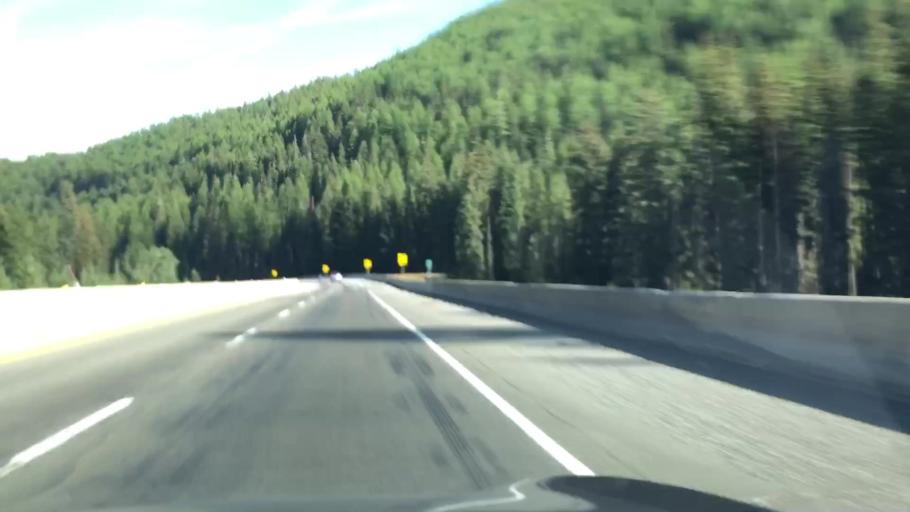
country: US
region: Idaho
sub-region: Shoshone County
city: Wallace
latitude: 47.4344
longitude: -115.6733
